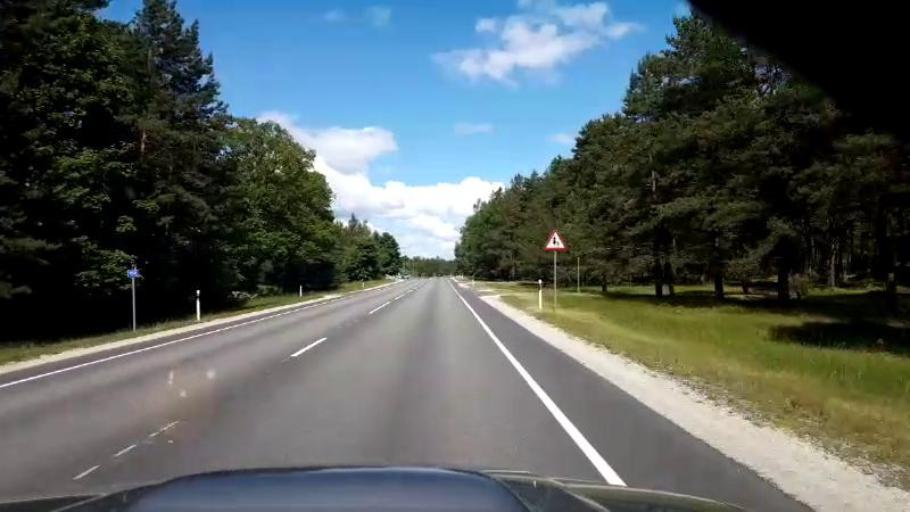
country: EE
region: Paernumaa
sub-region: Paernu linn
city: Parnu
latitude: 58.2067
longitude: 24.4854
